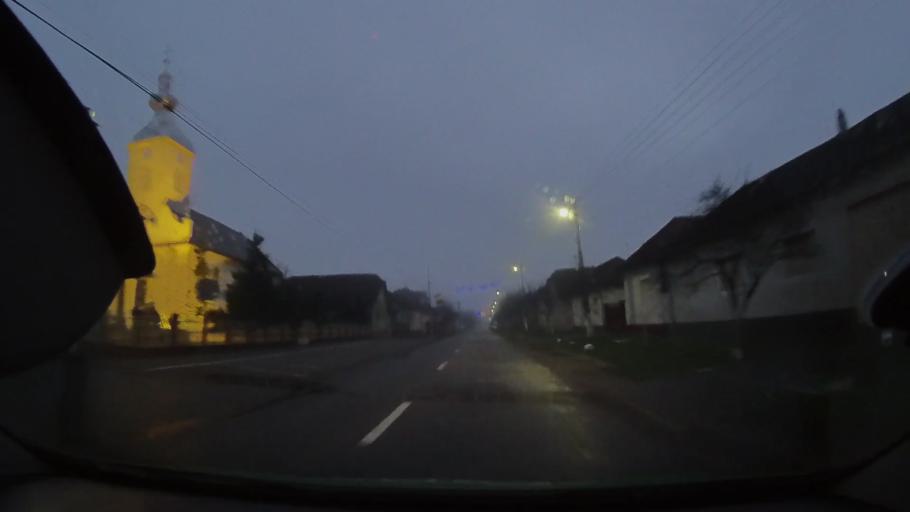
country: RO
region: Arad
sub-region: Comuna Archis
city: Archis
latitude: 46.4775
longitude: 22.0512
